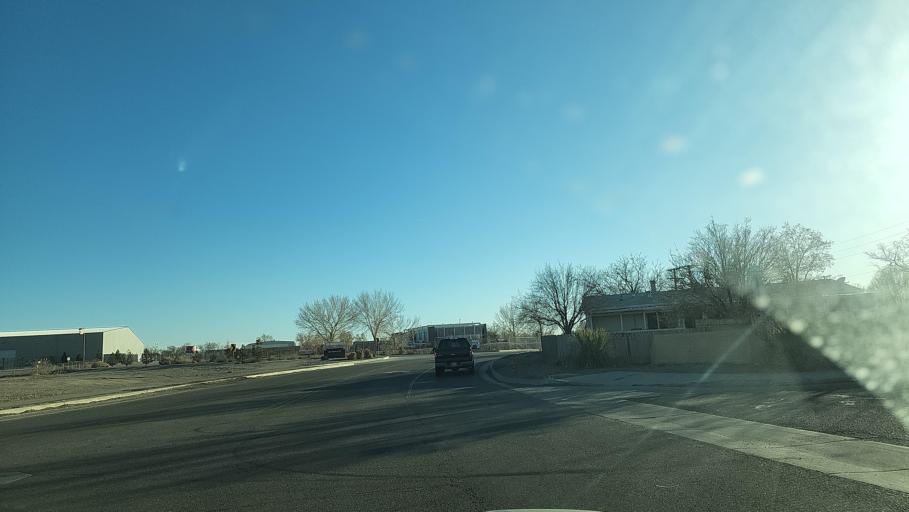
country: US
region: New Mexico
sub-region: Bernalillo County
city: South Valley
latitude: 35.0259
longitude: -106.6531
